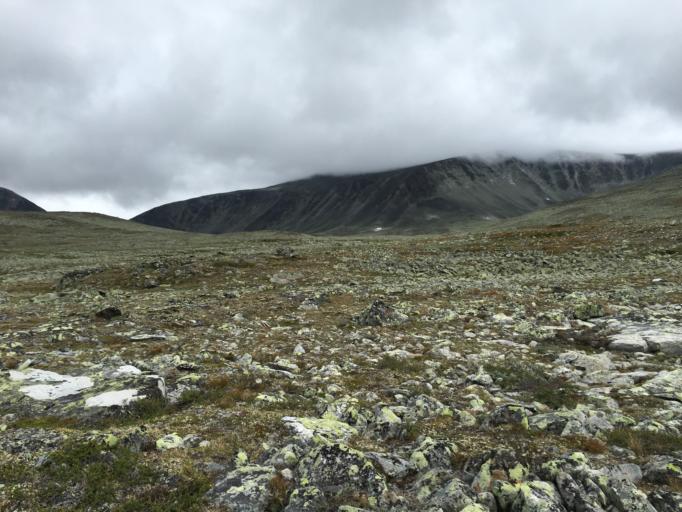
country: NO
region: Oppland
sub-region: Lom
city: Fossbergom
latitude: 61.5864
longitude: 8.7196
